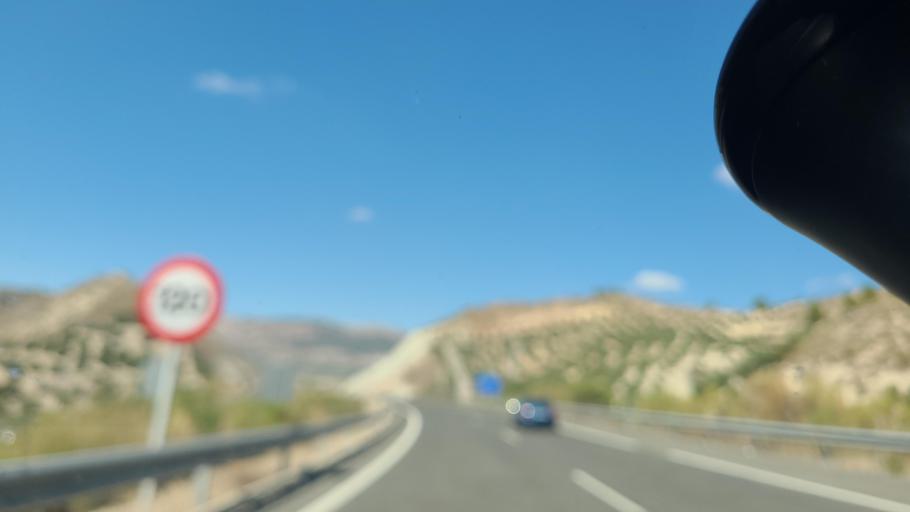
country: ES
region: Andalusia
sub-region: Provincia de Jaen
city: Pegalajar
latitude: 37.6938
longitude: -3.6314
